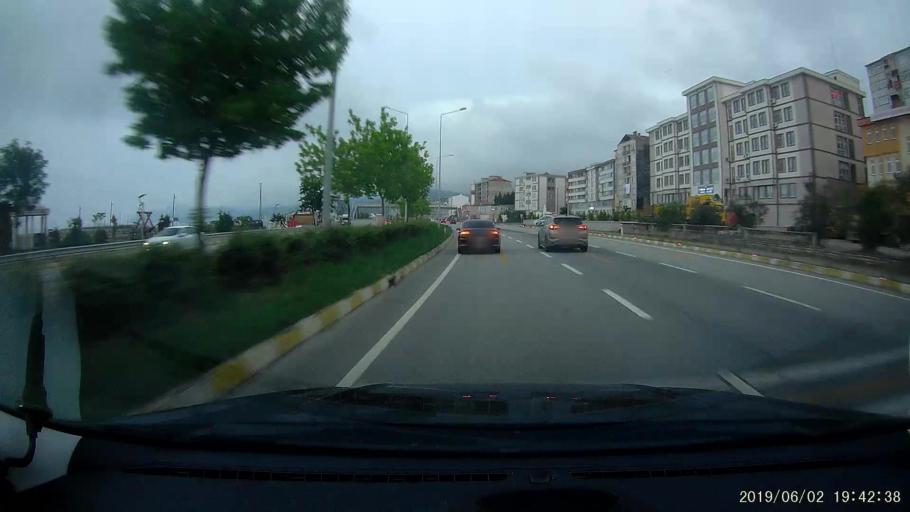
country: TR
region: Giresun
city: Kesap
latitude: 40.9172
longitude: 38.5095
